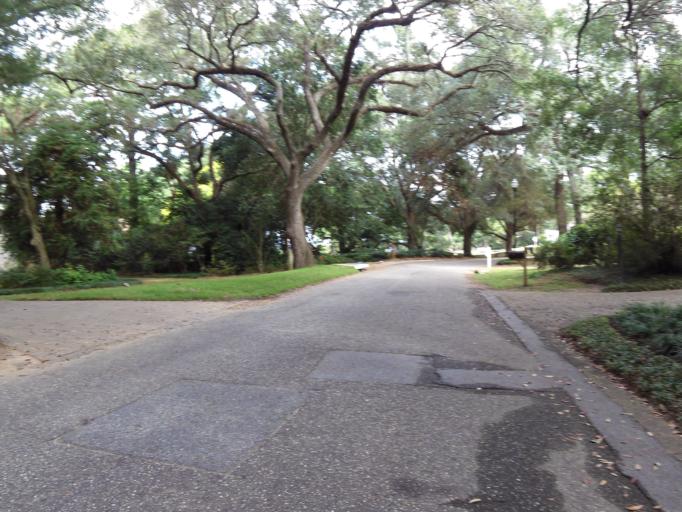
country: US
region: Alabama
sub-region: Baldwin County
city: Fairhope
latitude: 30.5259
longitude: -87.9083
